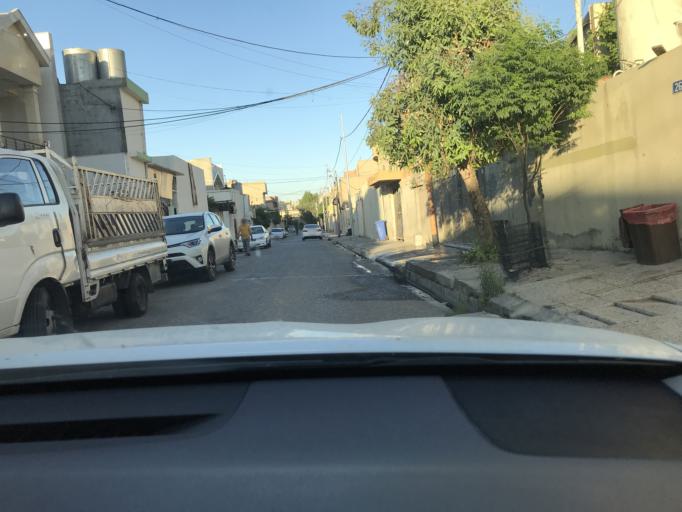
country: IQ
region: Arbil
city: Erbil
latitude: 36.2045
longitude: 44.0111
